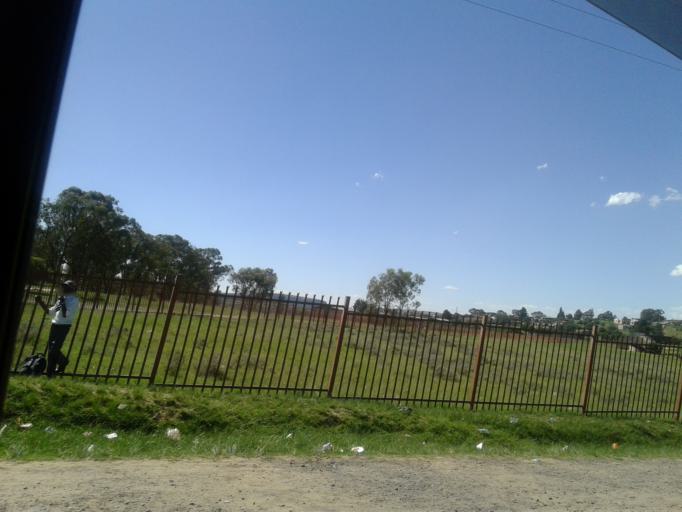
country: LS
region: Butha-Buthe
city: Butha-Buthe
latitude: -28.7611
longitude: 28.2561
